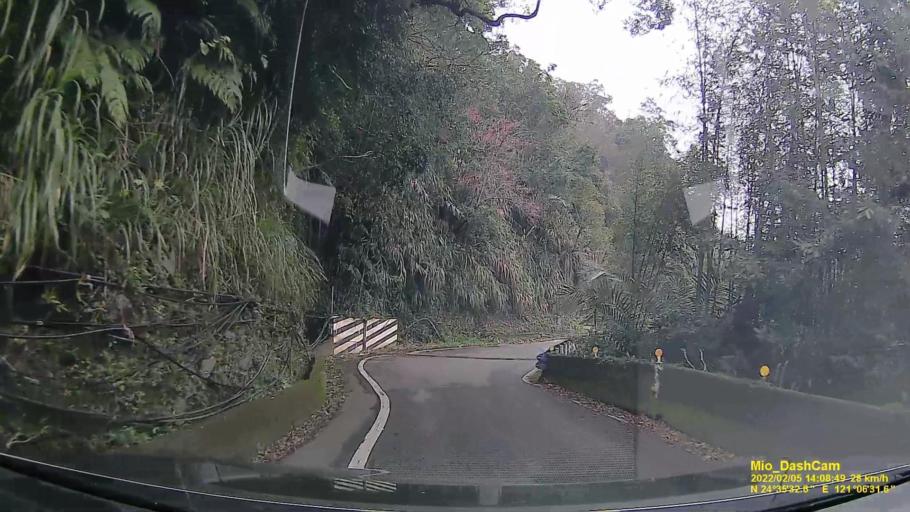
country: TW
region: Taiwan
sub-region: Hsinchu
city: Hsinchu
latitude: 24.5924
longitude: 121.1088
